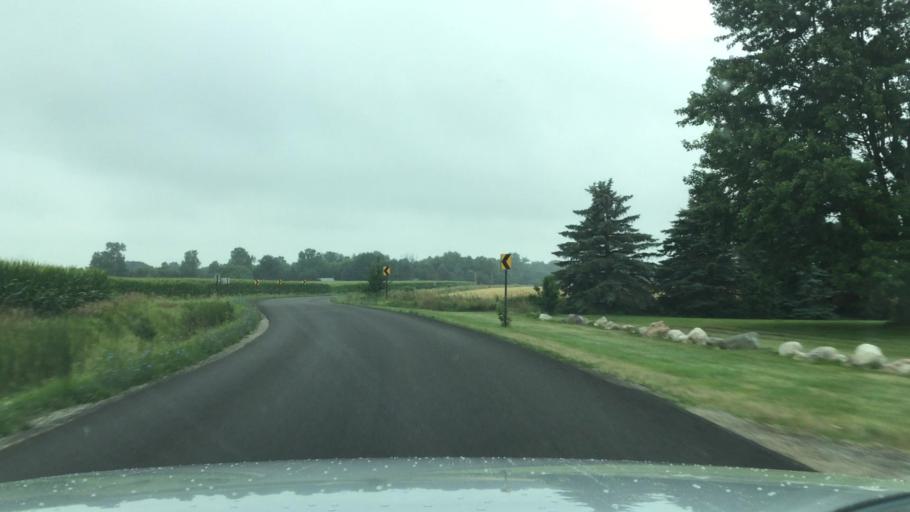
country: US
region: Michigan
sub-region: Shiawassee County
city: New Haven
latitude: 43.0571
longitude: -84.1663
